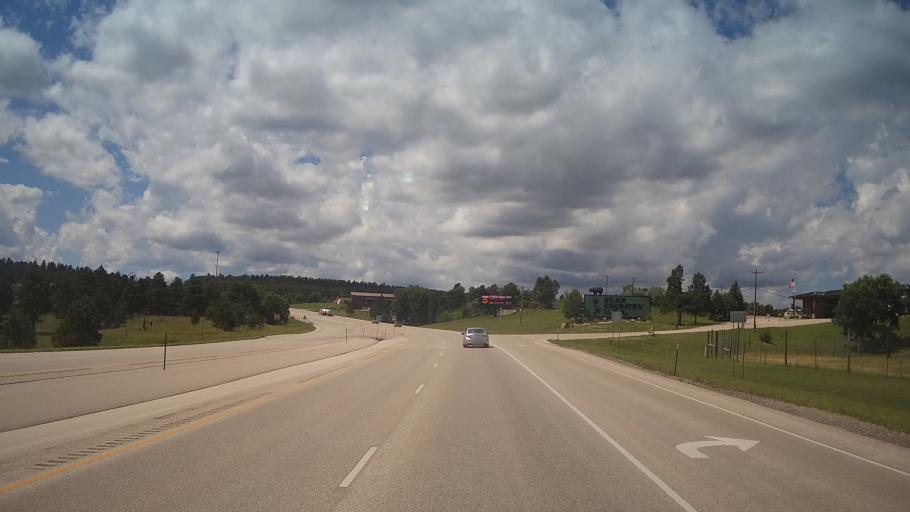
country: US
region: South Dakota
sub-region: Pennington County
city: Colonial Pine Hills
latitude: 43.9749
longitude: -103.2953
